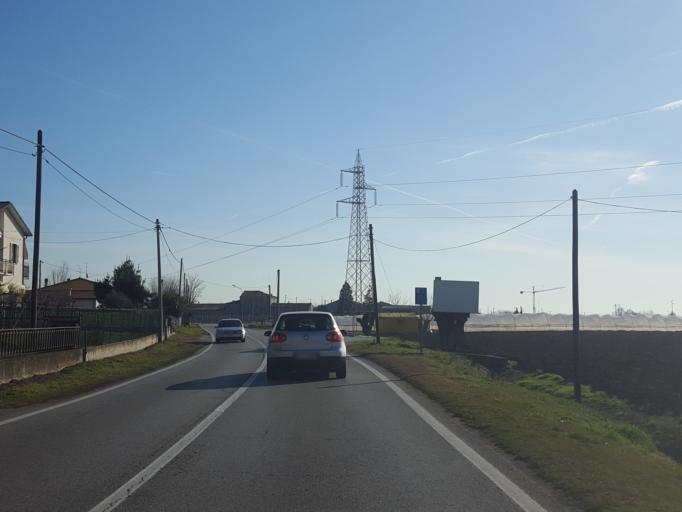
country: IT
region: Veneto
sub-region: Provincia di Verona
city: Locara
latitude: 45.3960
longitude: 11.3451
